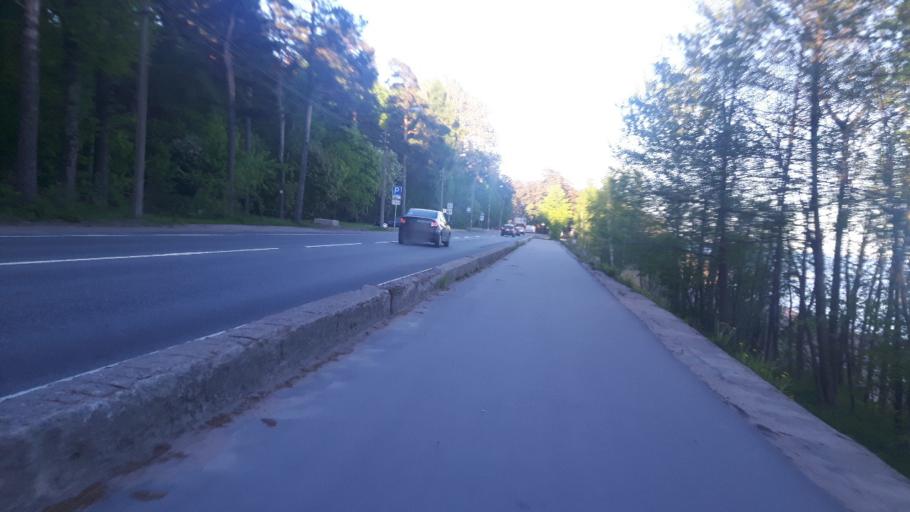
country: RU
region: St.-Petersburg
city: Zelenogorsk
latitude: 60.1917
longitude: 29.6432
